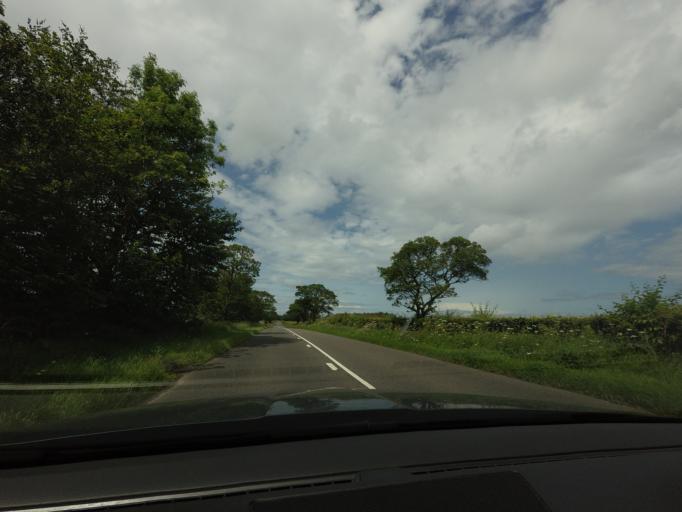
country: GB
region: Scotland
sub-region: Aberdeenshire
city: Portsoy
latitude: 57.6575
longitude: -2.6611
